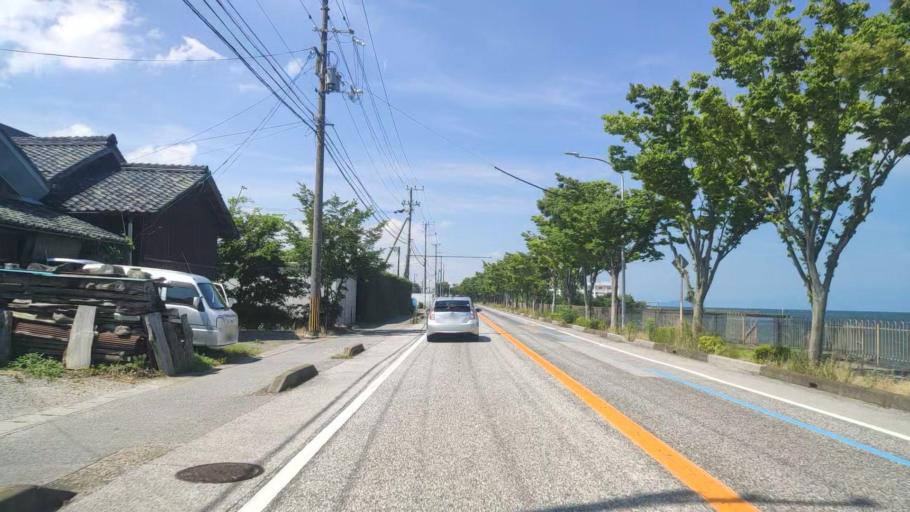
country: JP
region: Shiga Prefecture
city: Hikone
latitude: 35.2775
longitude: 136.2394
